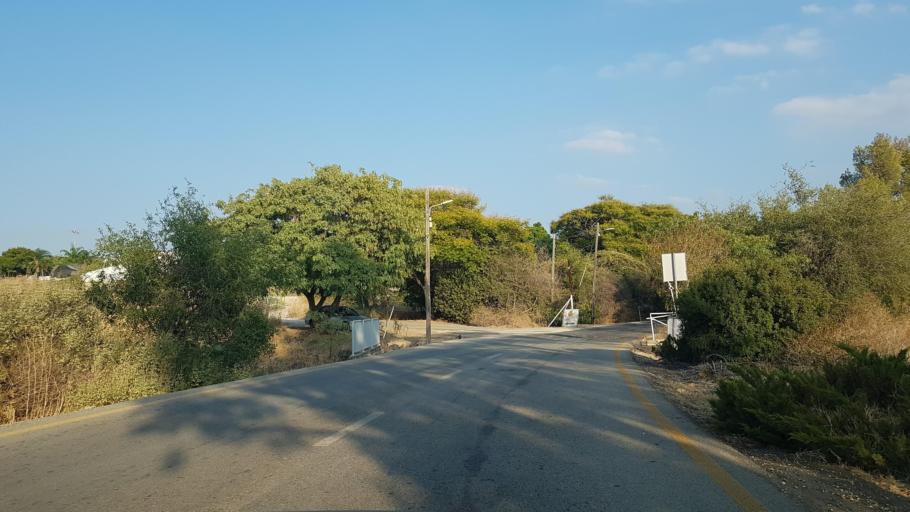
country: SY
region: Quneitra
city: Al Butayhah
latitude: 32.9137
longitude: 35.5994
